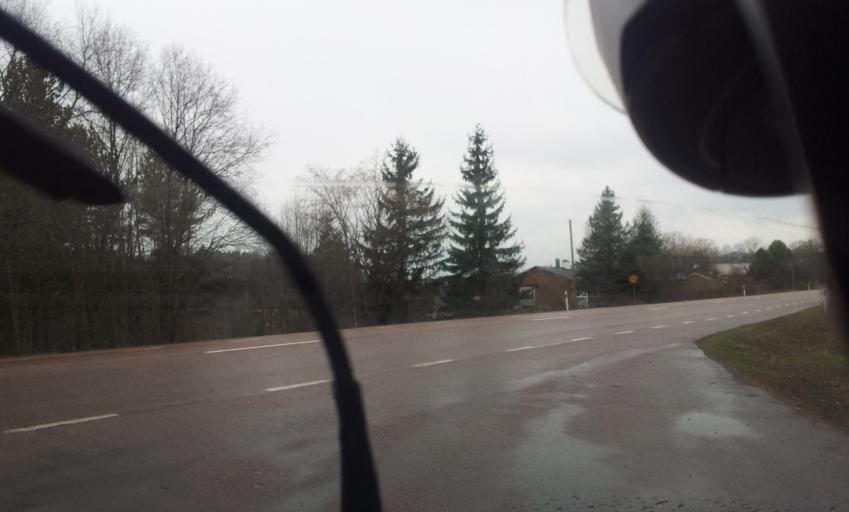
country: SE
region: Dalarna
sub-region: Gagnefs Kommun
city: Djuras
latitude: 60.5494
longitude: 15.2688
